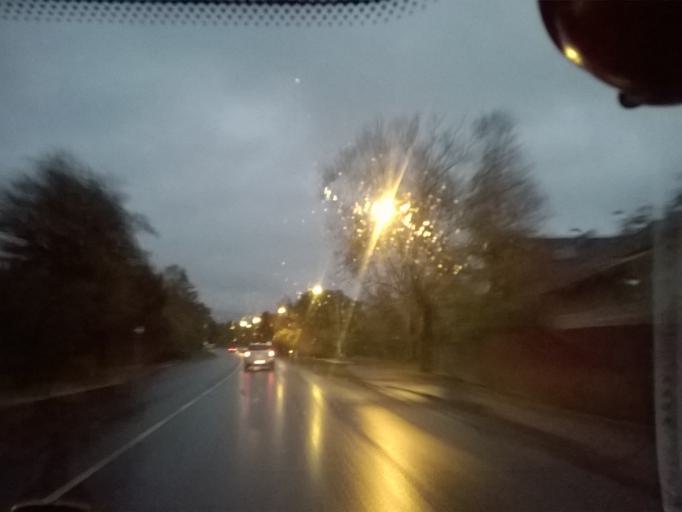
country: EE
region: Harju
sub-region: Viimsi vald
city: Rummu
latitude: 59.5212
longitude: 24.8052
